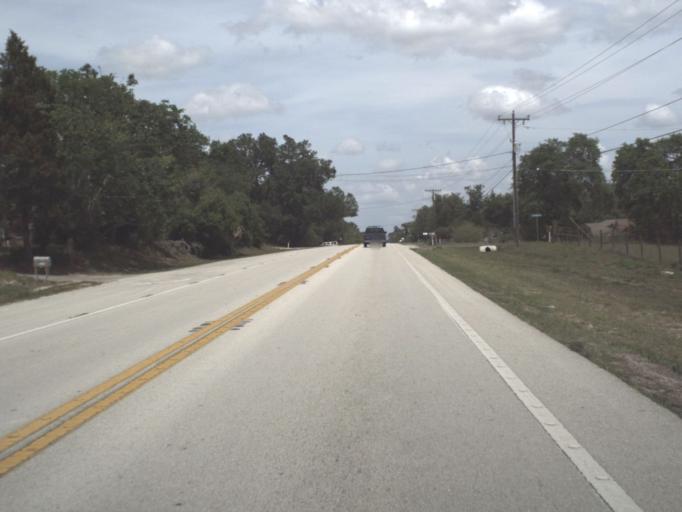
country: US
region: Florida
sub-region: Lake County
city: Lake Mack-Forest Hills
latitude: 28.9470
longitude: -81.4254
